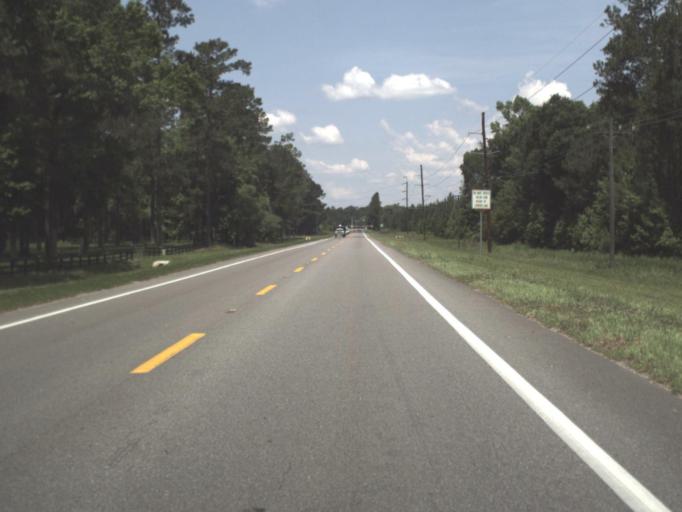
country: US
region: Florida
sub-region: Union County
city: Lake Butler
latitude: 30.0189
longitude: -82.3150
